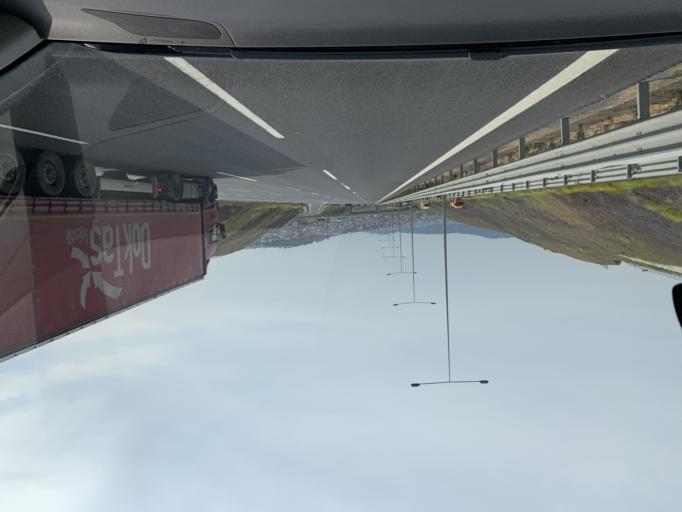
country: TR
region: Istanbul
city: Sancaktepe
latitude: 41.0338
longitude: 29.2729
